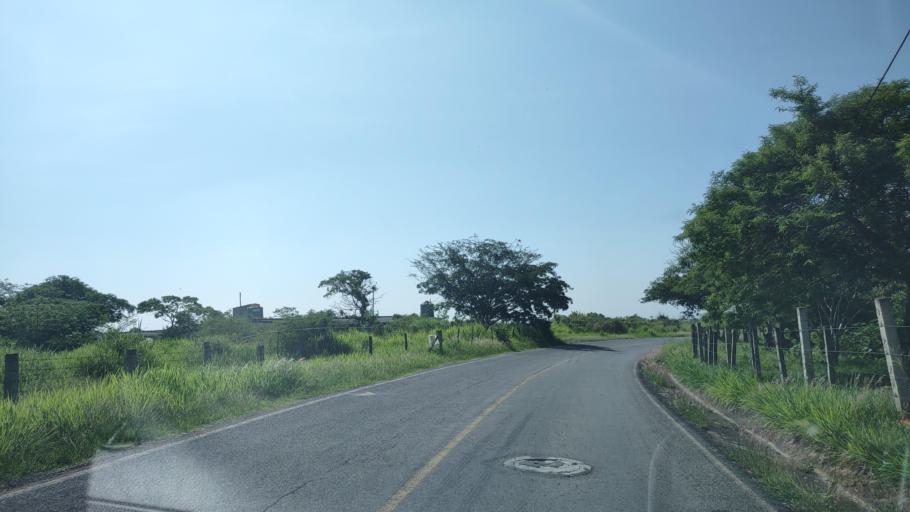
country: MX
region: Veracruz
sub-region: Emiliano Zapata
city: Dos Rios
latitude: 19.4939
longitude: -96.8239
